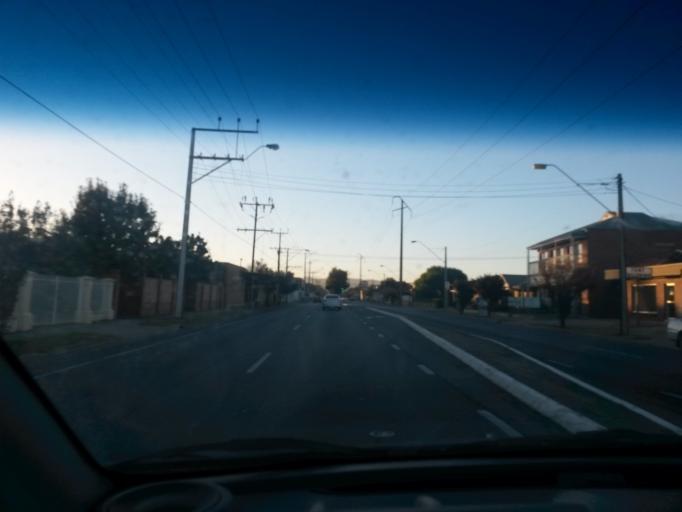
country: AU
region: South Australia
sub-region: Charles Sturt
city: Woodville
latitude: -34.8778
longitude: 138.5527
